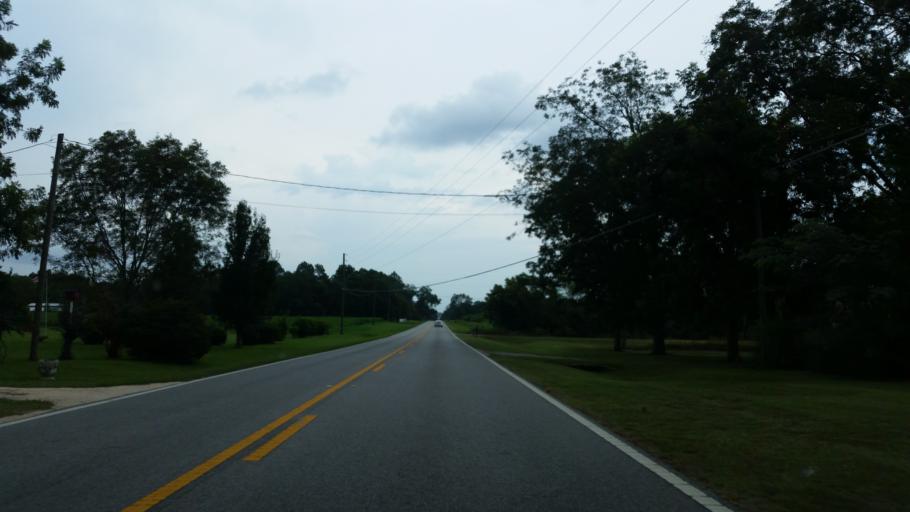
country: US
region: Florida
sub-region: Escambia County
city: Molino
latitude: 30.6809
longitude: -87.3733
